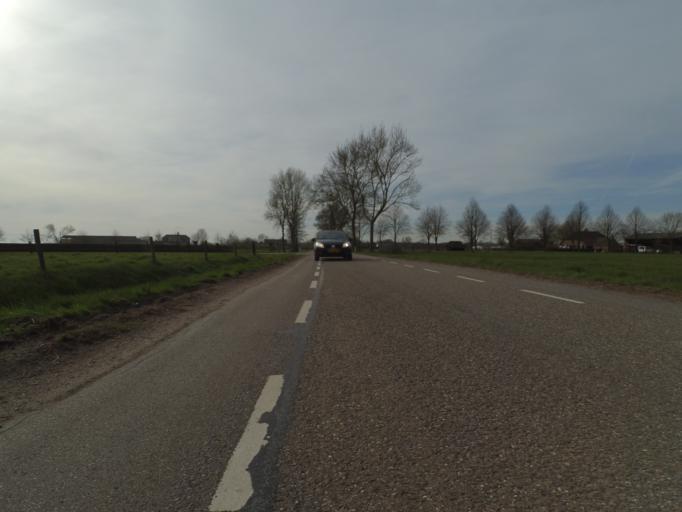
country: NL
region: Gelderland
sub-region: Gemeente Ede
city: Lunteren
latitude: 52.0641
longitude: 5.6067
